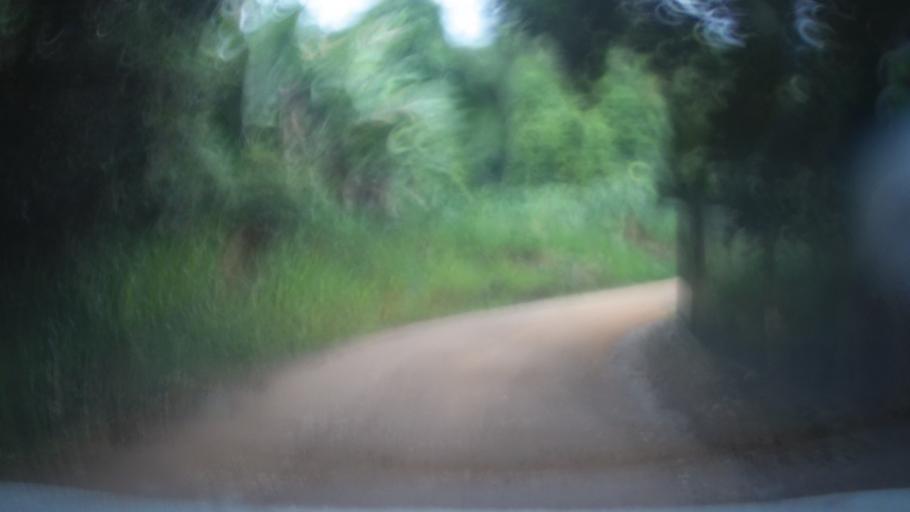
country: BR
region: Sao Paulo
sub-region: Itupeva
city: Itupeva
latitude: -23.1651
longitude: -47.0664
